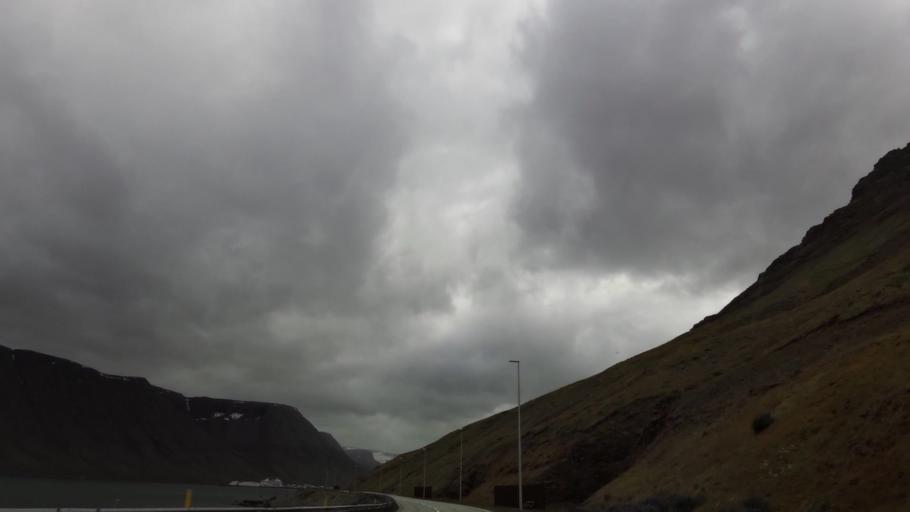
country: IS
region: Westfjords
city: Isafjoerdur
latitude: 66.0953
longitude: -23.1123
